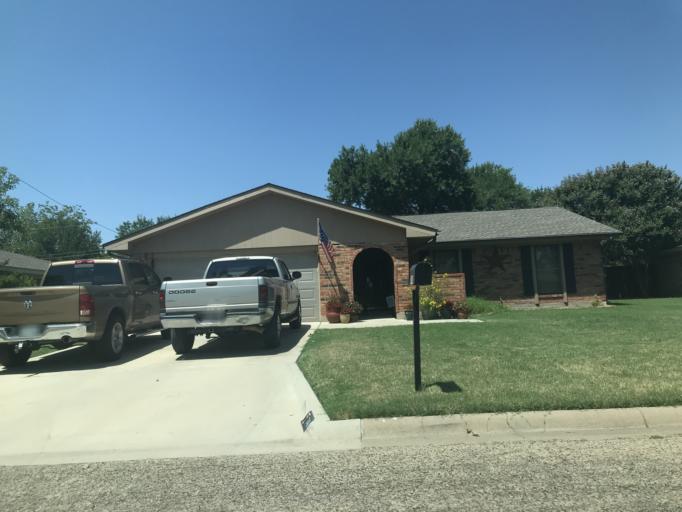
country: US
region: Texas
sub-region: Taylor County
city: Abilene
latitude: 32.4554
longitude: -99.7003
